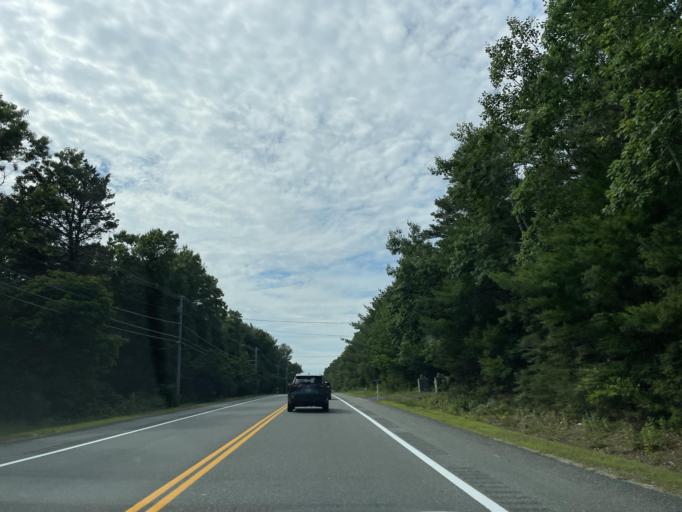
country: US
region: Rhode Island
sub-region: Kent County
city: West Greenwich
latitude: 41.6162
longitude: -71.6702
